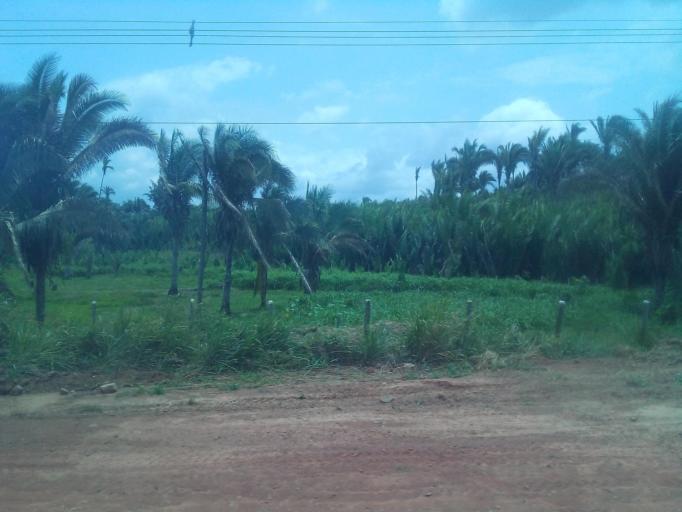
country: BR
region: Maranhao
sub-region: Santa Ines
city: Santa Ines
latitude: -3.6954
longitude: -45.6215
